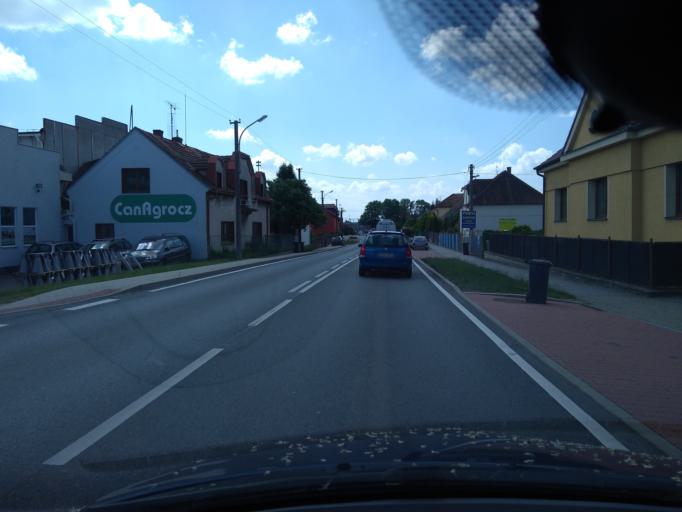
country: CZ
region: Plzensky
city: Chlumcany
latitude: 49.6153
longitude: 13.3255
